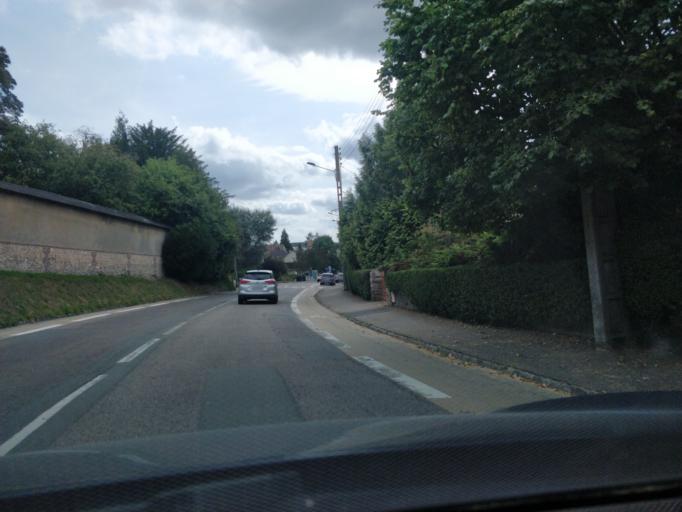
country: FR
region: Haute-Normandie
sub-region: Departement de la Seine-Maritime
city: Bois-Guillaume
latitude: 49.4739
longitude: 1.1127
